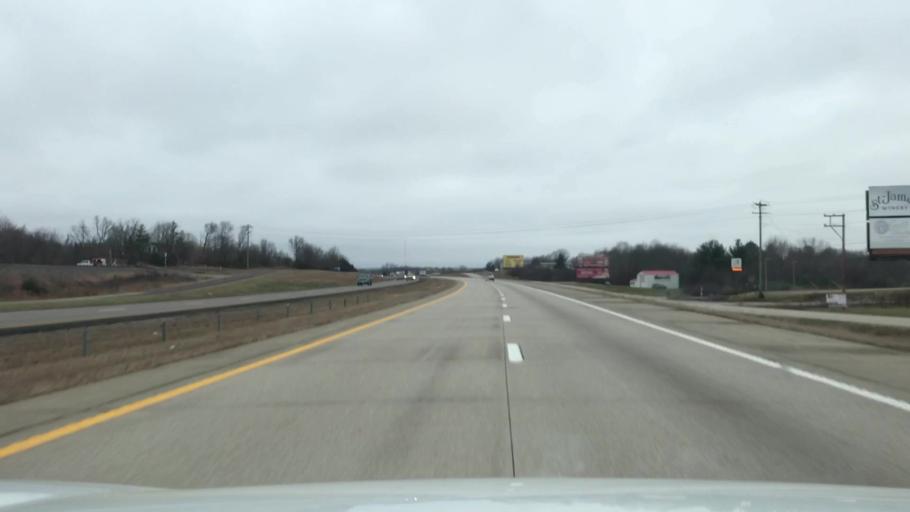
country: US
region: Missouri
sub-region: Crawford County
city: Bourbon
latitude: 38.1791
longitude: -91.2073
